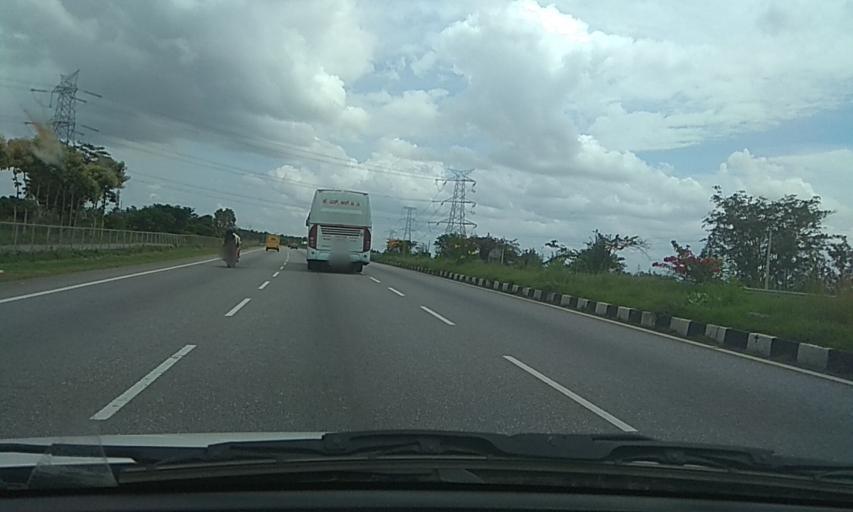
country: IN
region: Karnataka
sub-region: Tumkur
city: Tumkur
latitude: 13.4963
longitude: 77.0120
